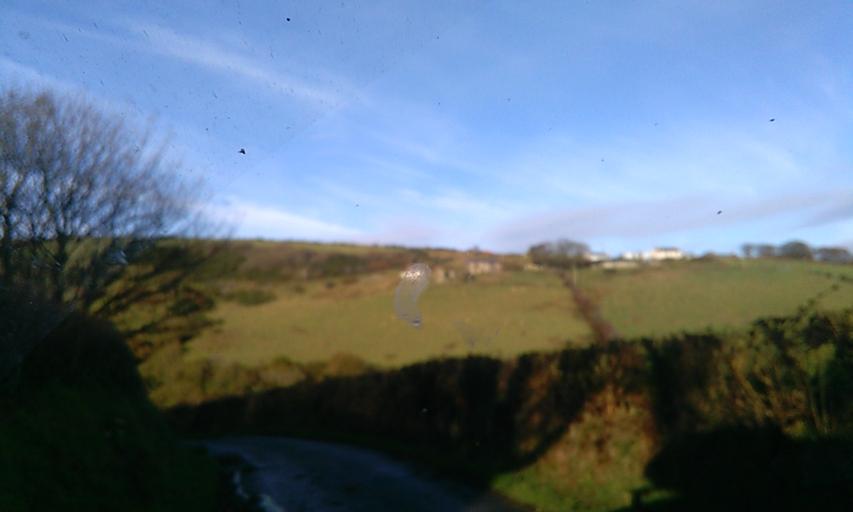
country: IE
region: Ulster
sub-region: County Donegal
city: Moville
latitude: 55.2489
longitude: -7.0020
